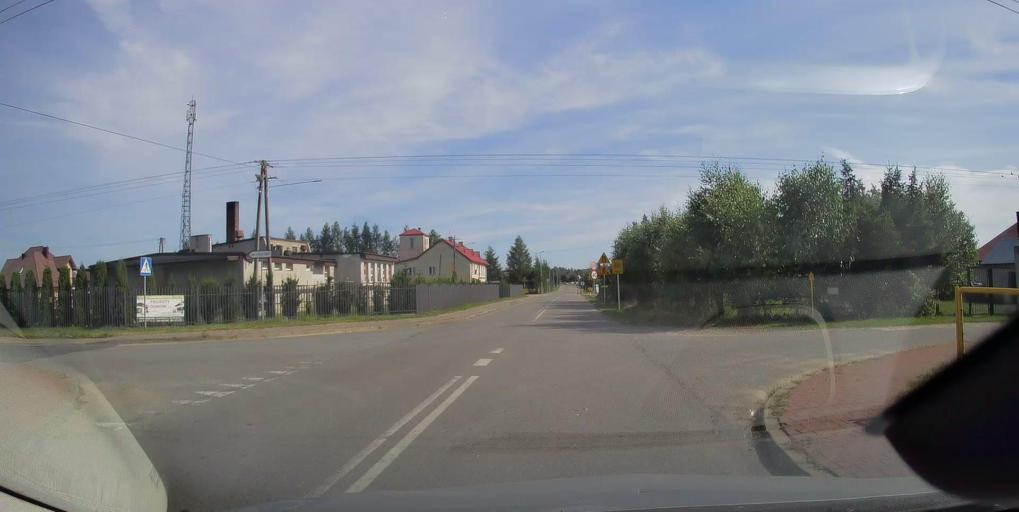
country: PL
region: Lodz Voivodeship
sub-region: Powiat opoczynski
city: Mniszkow
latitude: 51.3735
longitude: 20.0385
